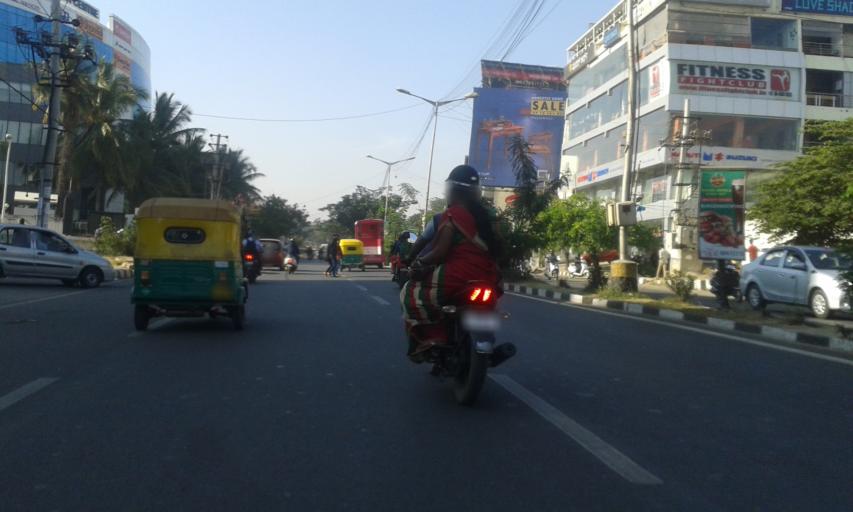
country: IN
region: Karnataka
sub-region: Bangalore Urban
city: Bangalore
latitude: 12.9530
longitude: 77.6407
